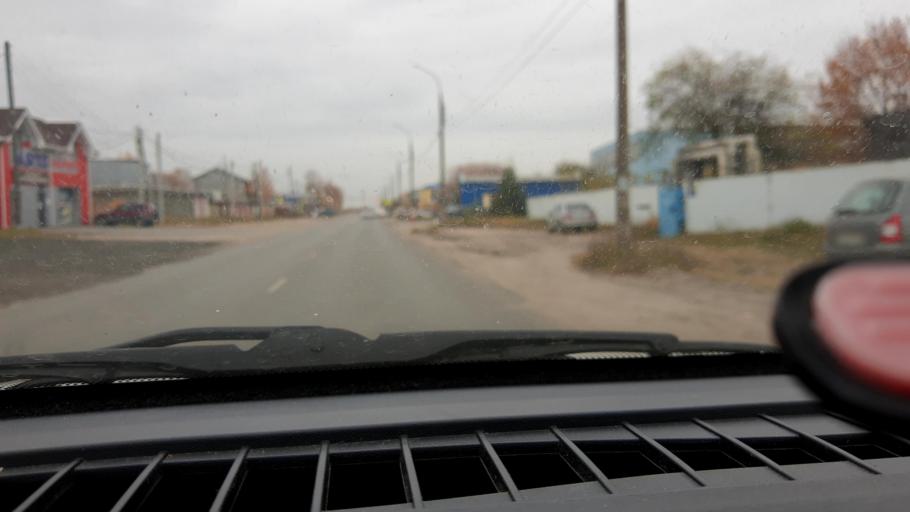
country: RU
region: Nizjnij Novgorod
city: Gorodets
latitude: 56.6432
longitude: 43.4894
